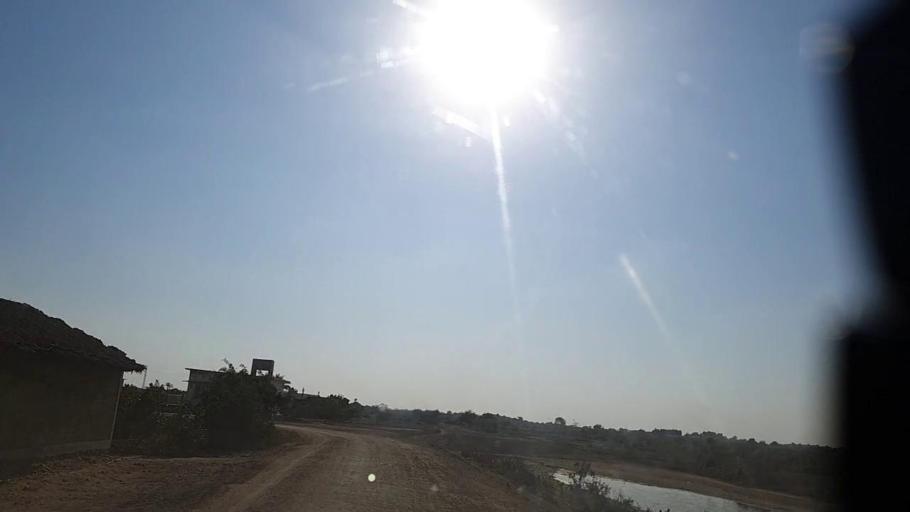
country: PK
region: Sindh
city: Digri
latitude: 25.1520
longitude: 69.0393
